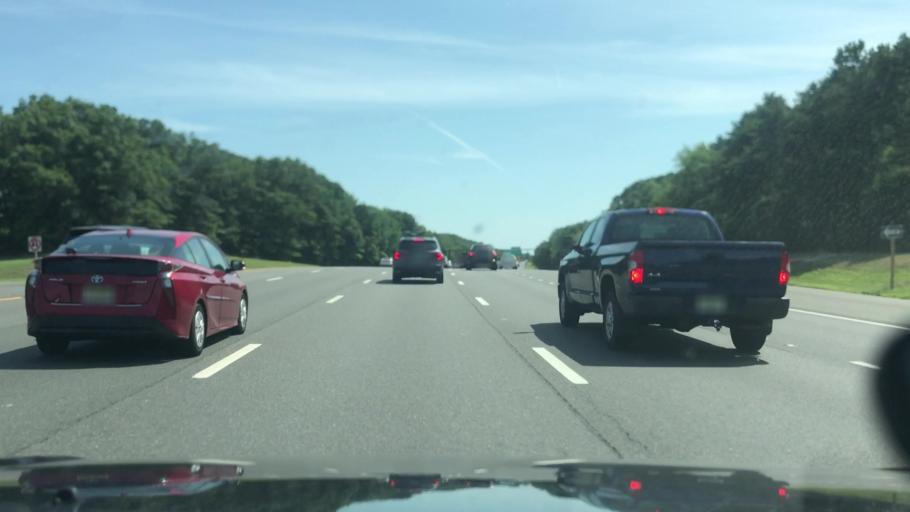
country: US
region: New Jersey
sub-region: Monmouth County
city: Eatontown
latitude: 40.2480
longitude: -74.0832
